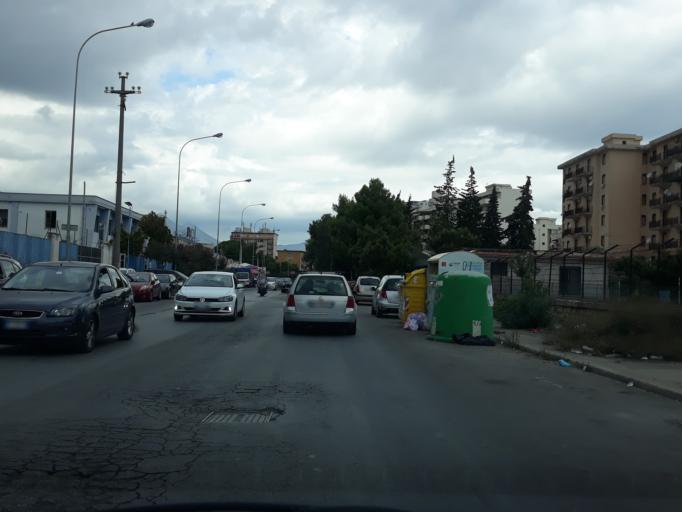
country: IT
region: Sicily
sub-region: Palermo
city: Ciaculli
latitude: 38.0962
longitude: 13.3956
